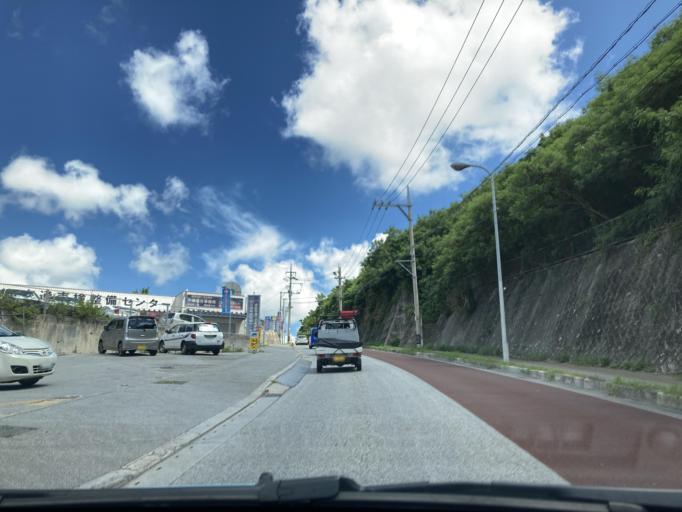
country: JP
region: Okinawa
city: Naha-shi
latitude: 26.2099
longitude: 127.7236
